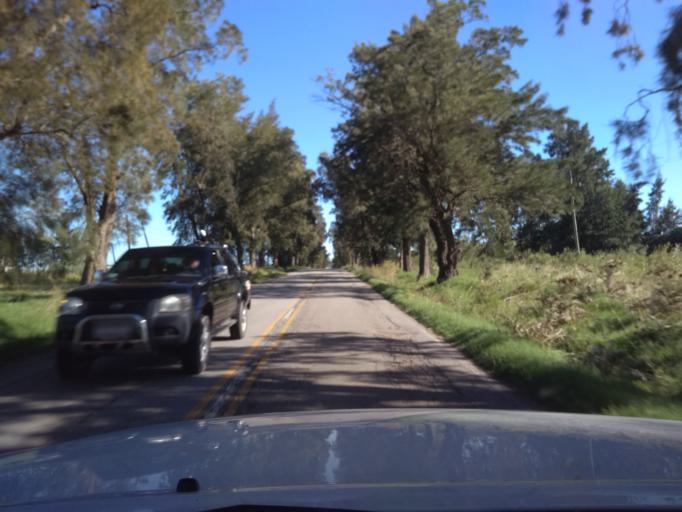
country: UY
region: Canelones
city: San Ramon
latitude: -34.3684
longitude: -55.9595
